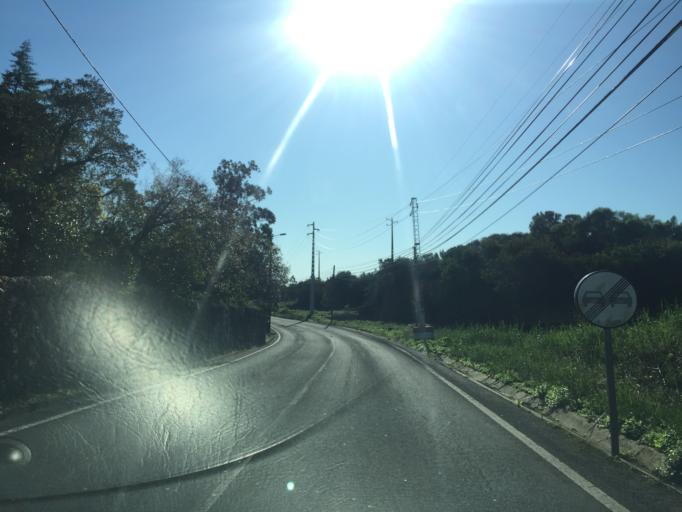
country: PT
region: Lisbon
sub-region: Sintra
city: Belas
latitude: 38.7902
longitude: -9.2673
